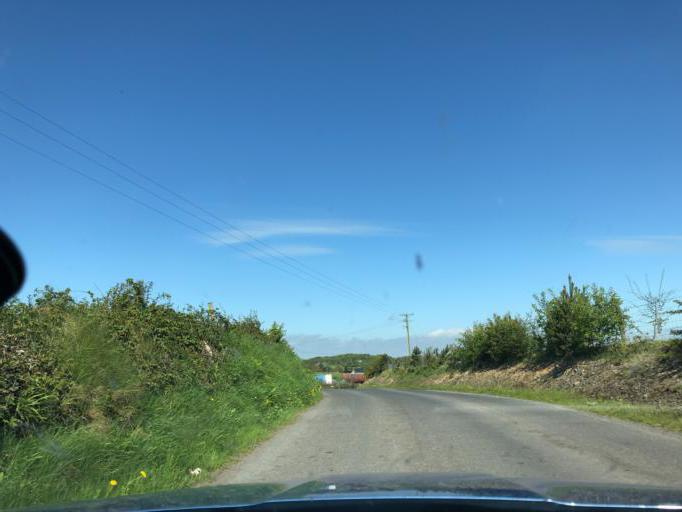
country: IE
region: Connaught
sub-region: County Galway
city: Portumna
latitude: 53.1558
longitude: -8.2946
